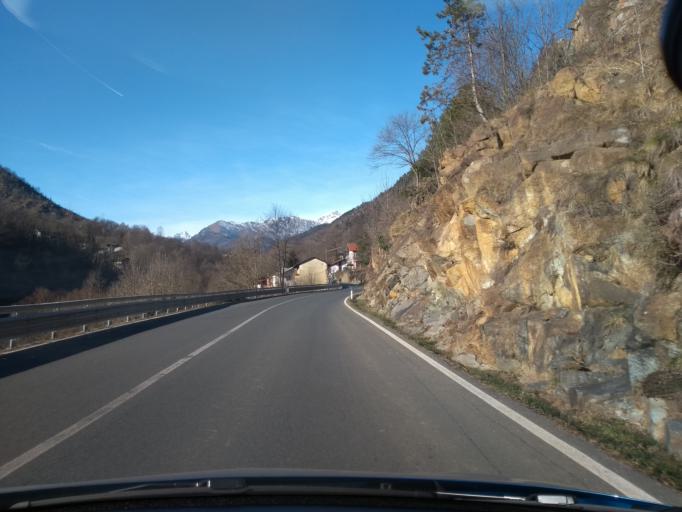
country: IT
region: Piedmont
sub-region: Provincia di Torino
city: La Villa
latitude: 45.2358
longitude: 7.4316
